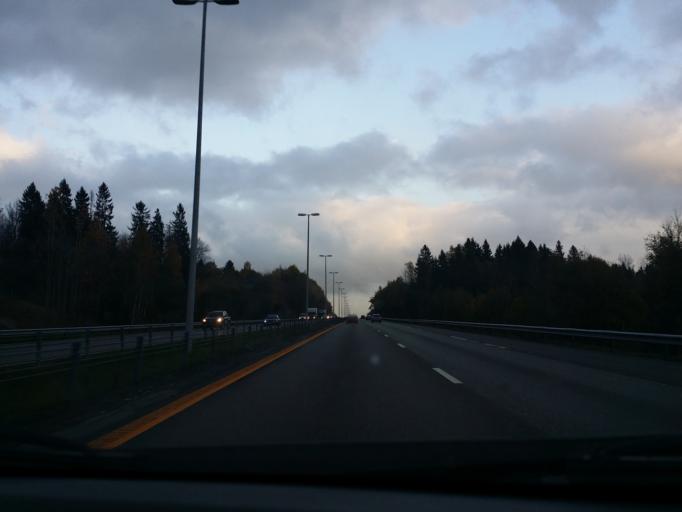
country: NO
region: Akershus
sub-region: Asker
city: Asker
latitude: 59.8246
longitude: 10.3651
